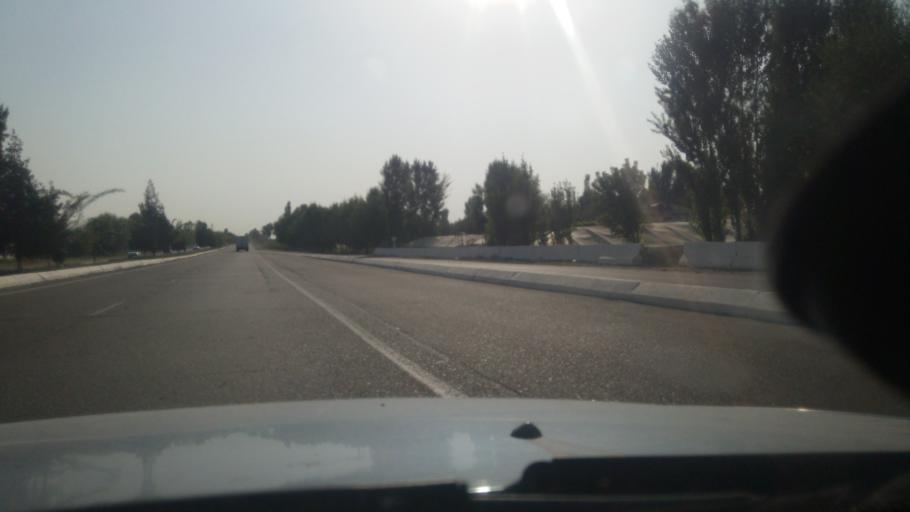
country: UZ
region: Toshkent
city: Zafar
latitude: 41.0090
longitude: 68.8355
